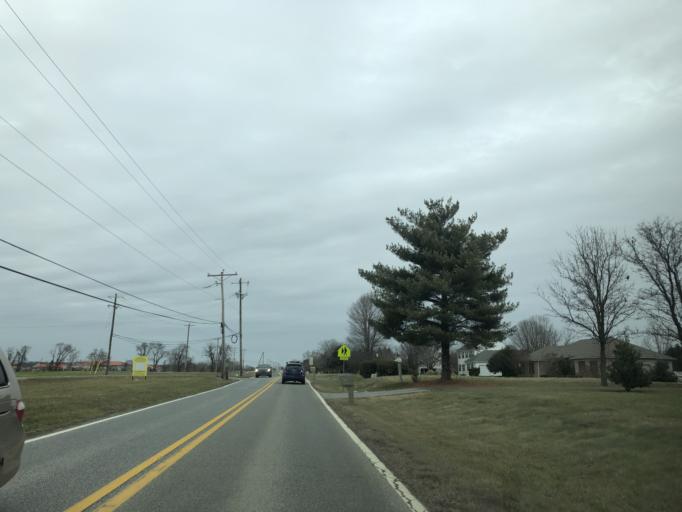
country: US
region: Delaware
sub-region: New Castle County
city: Middletown
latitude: 39.4962
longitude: -75.6878
